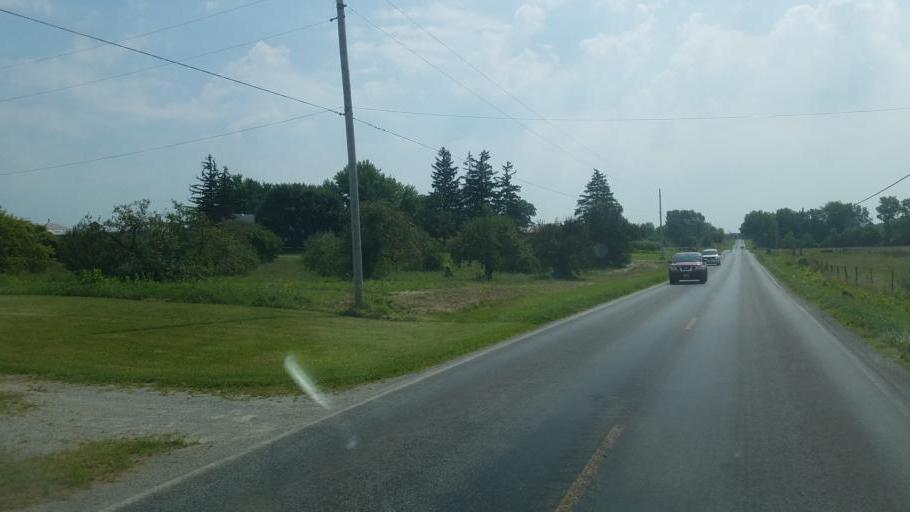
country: US
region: Ohio
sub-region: Hardin County
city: Kenton
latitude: 40.6219
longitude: -83.4920
